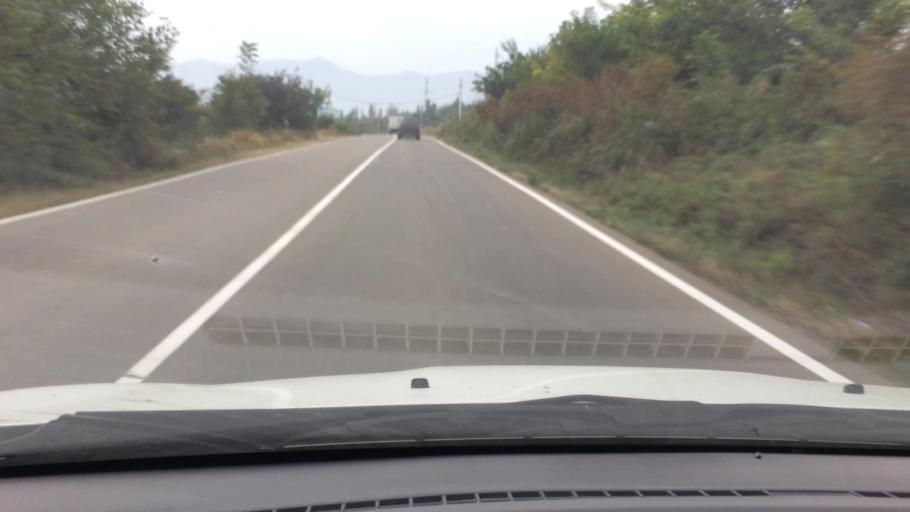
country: AM
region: Tavush
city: Bagratashen
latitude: 41.2693
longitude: 44.7910
